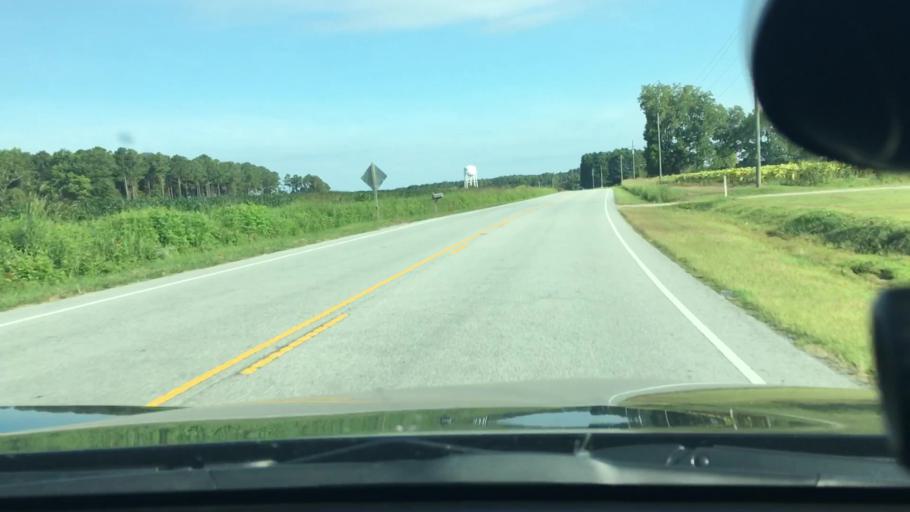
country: US
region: North Carolina
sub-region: Pitt County
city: Farmville
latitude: 35.7040
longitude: -77.5174
